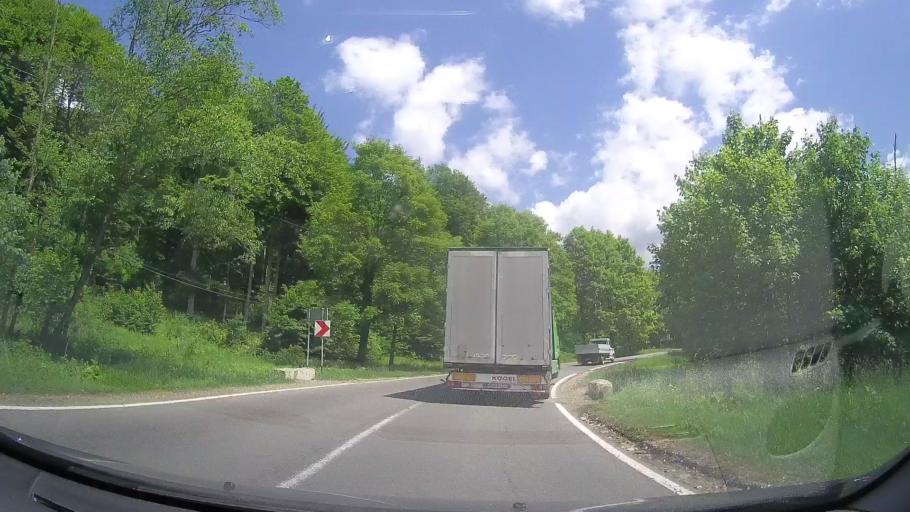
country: RO
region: Prahova
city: Maneciu
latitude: 45.4099
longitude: 25.9405
